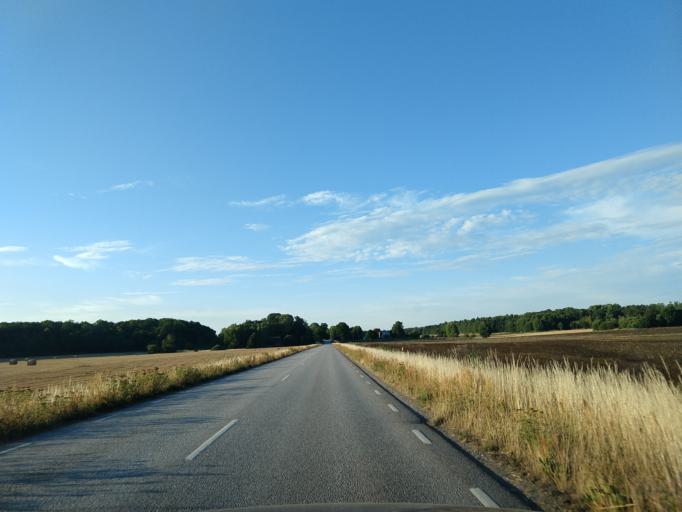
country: SE
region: Blekinge
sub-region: Ronneby Kommun
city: Brakne-Hoby
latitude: 56.2480
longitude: 15.1151
